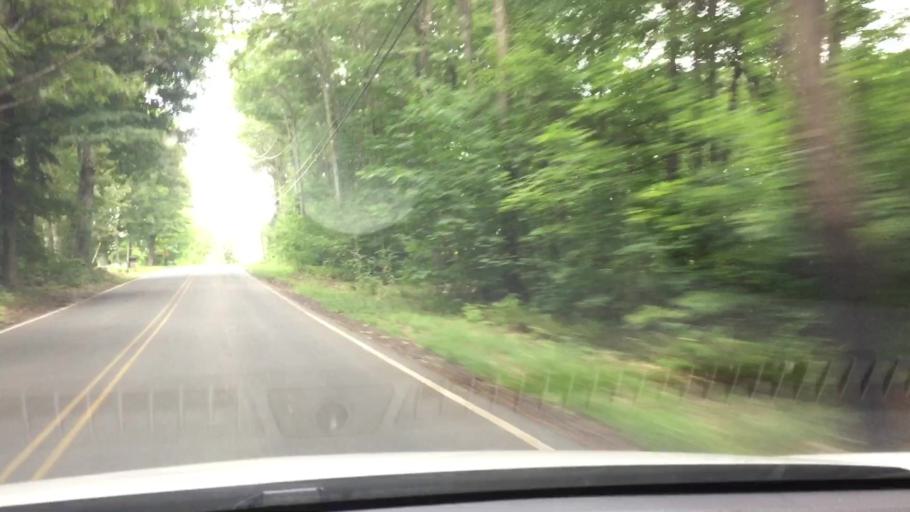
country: US
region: Massachusetts
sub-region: Berkshire County
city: Otis
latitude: 42.2166
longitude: -72.9510
